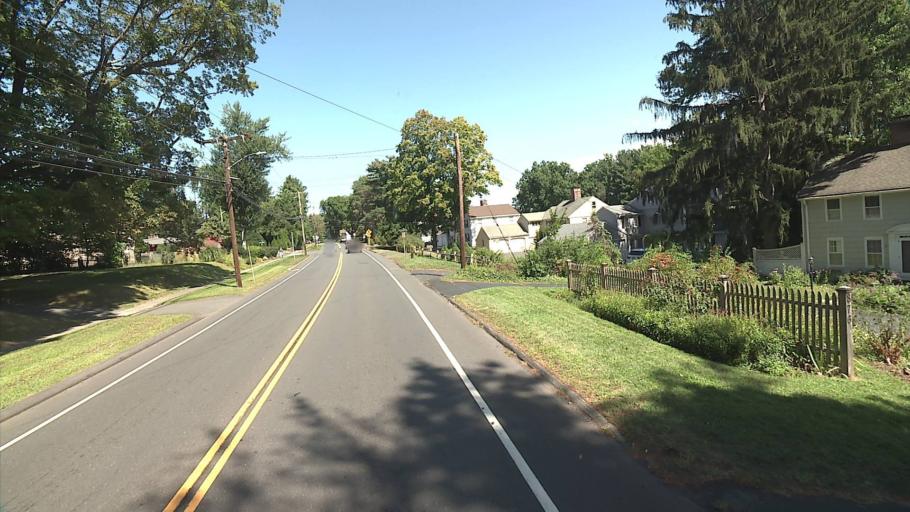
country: US
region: Connecticut
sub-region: Hartford County
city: West Hartford
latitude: 41.7912
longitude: -72.7467
